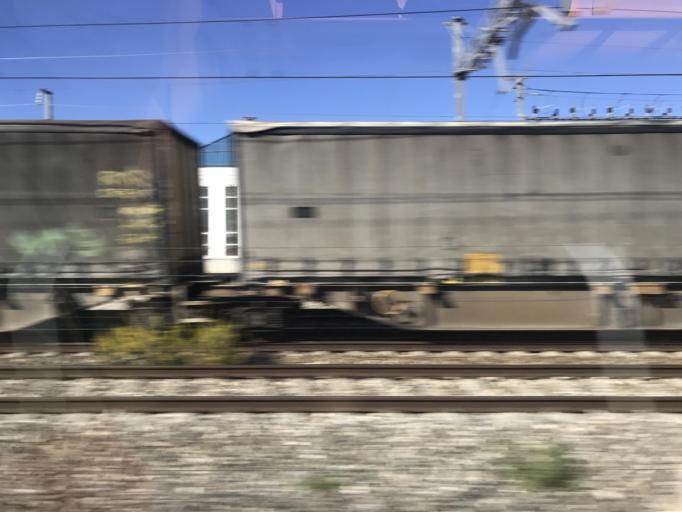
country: ES
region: Madrid
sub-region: Provincia de Madrid
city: Las Tablas
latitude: 40.4966
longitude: -3.6785
